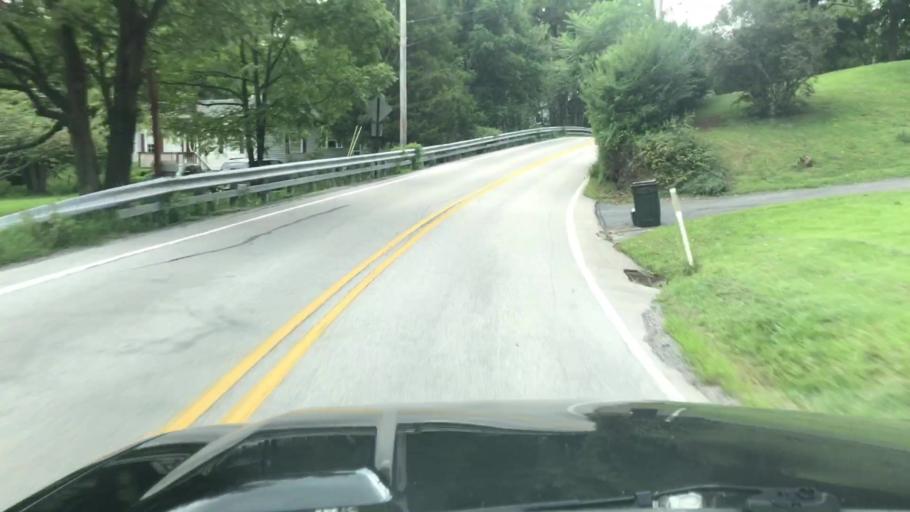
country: US
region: Pennsylvania
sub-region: Dauphin County
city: Steelton
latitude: 40.1808
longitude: -76.8569
